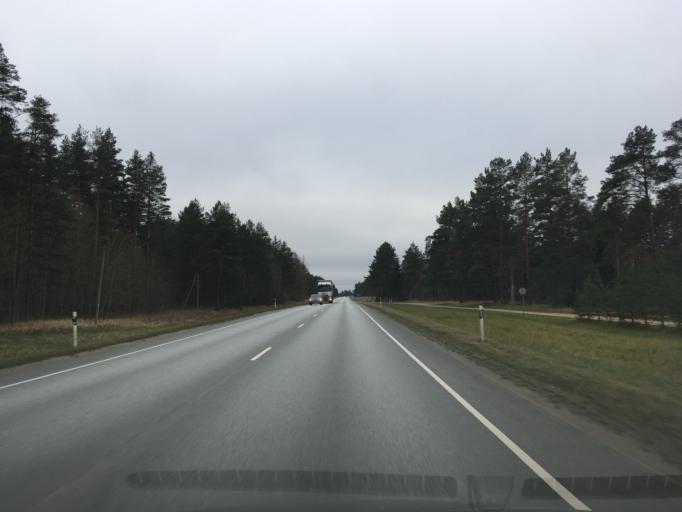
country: EE
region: Laeaene-Virumaa
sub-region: Viru-Nigula vald
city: Kunda
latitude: 59.4029
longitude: 26.6331
